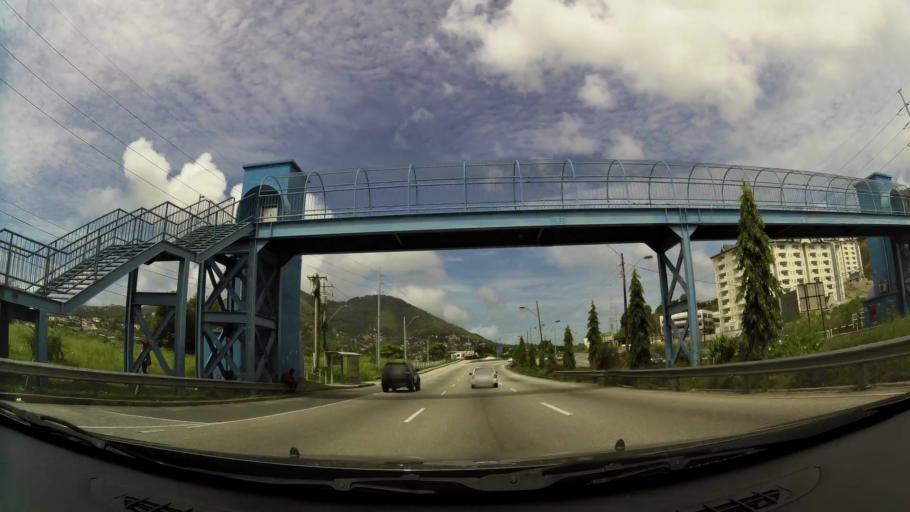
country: TT
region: City of Port of Spain
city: Mucurapo
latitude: 10.6805
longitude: -61.5528
